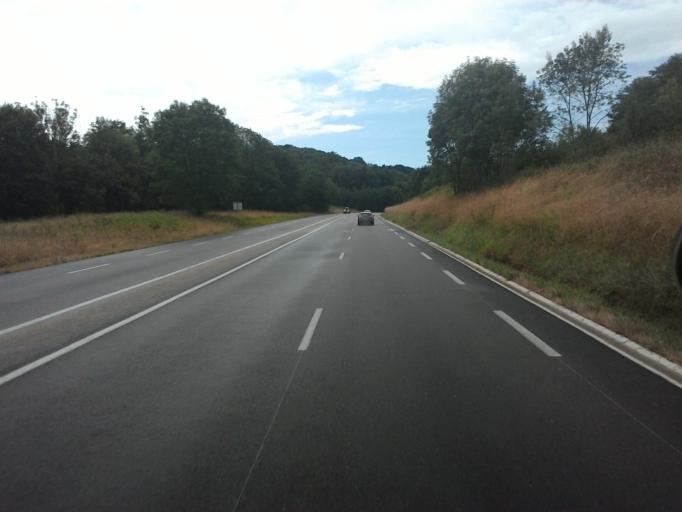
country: FR
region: Franche-Comte
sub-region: Departement du Jura
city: Bletterans
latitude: 46.7975
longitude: 5.5708
